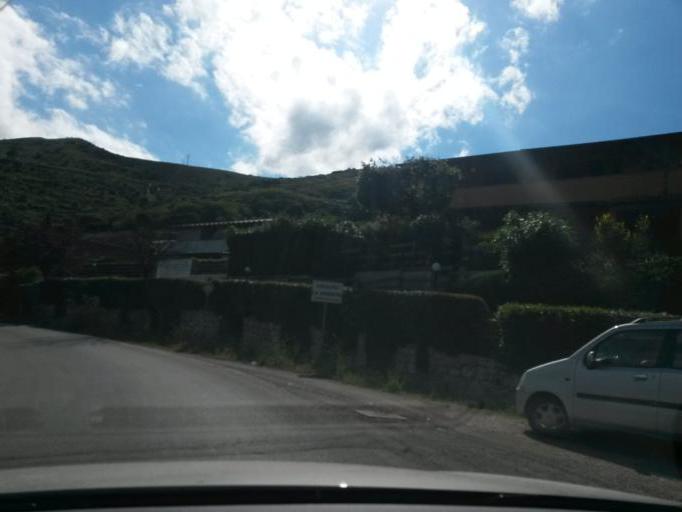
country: IT
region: Tuscany
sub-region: Provincia di Livorno
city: Rio nell'Elba
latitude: 42.8097
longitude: 10.4021
